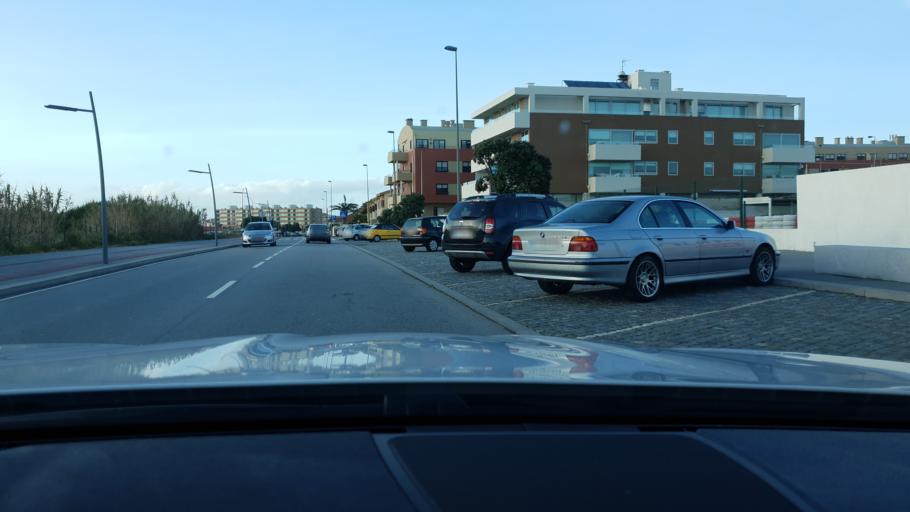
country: PT
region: Porto
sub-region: Matosinhos
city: Santa Cruz do Bispo
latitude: 41.2227
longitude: -8.7147
